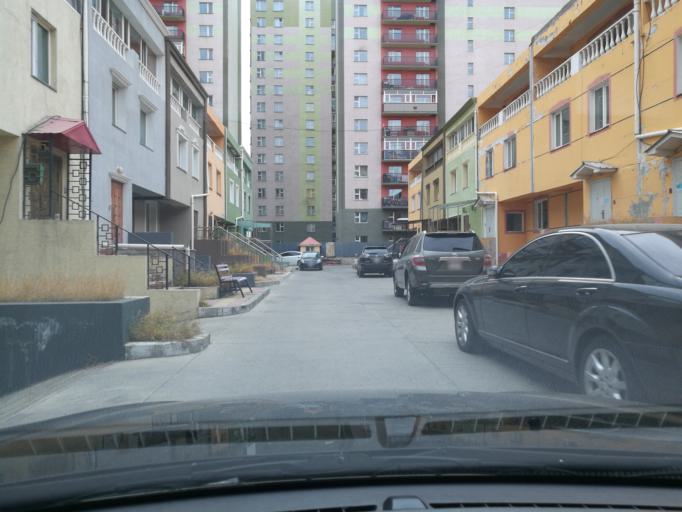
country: MN
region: Ulaanbaatar
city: Ulaanbaatar
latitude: 47.9040
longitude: 106.9265
